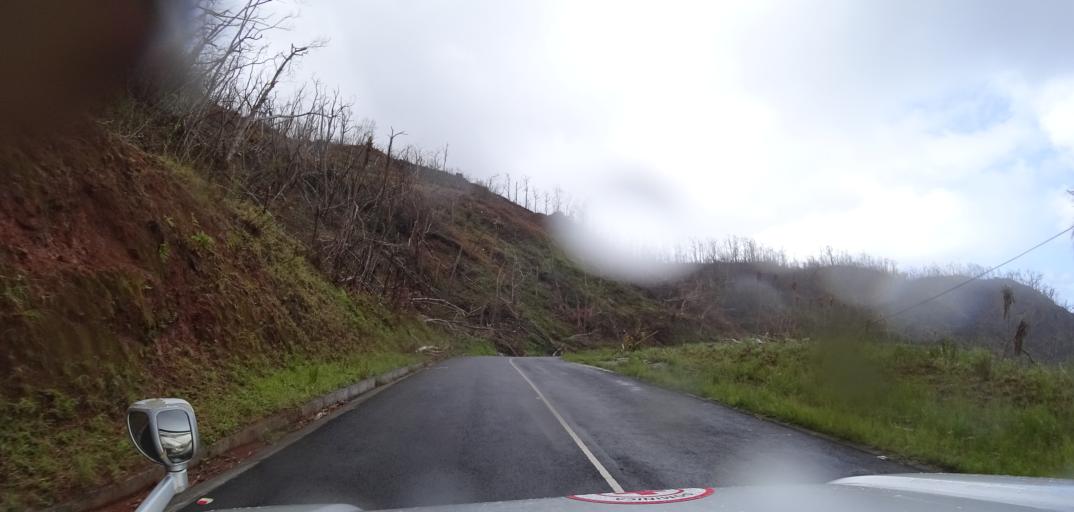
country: DM
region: Saint Andrew
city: Marigot
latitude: 15.5091
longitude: -61.2800
